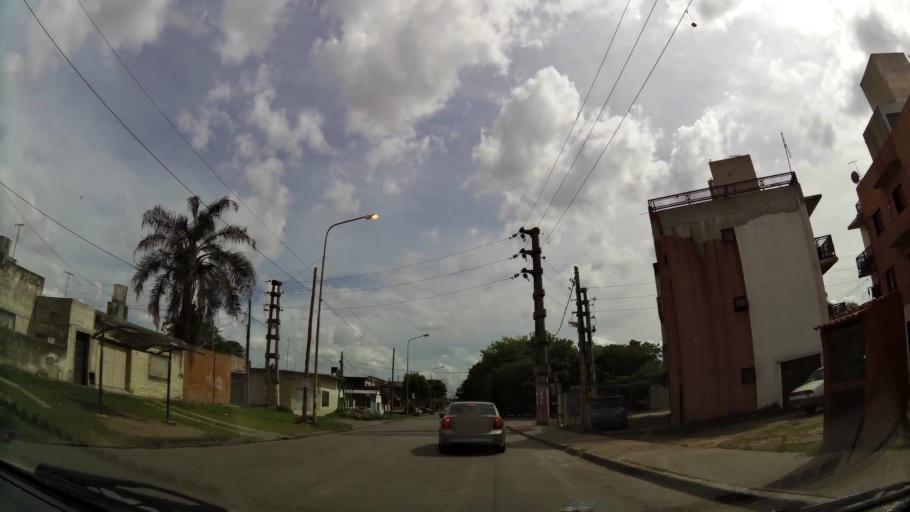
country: AR
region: Buenos Aires
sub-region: Partido de Quilmes
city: Quilmes
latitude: -34.7544
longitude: -58.2496
